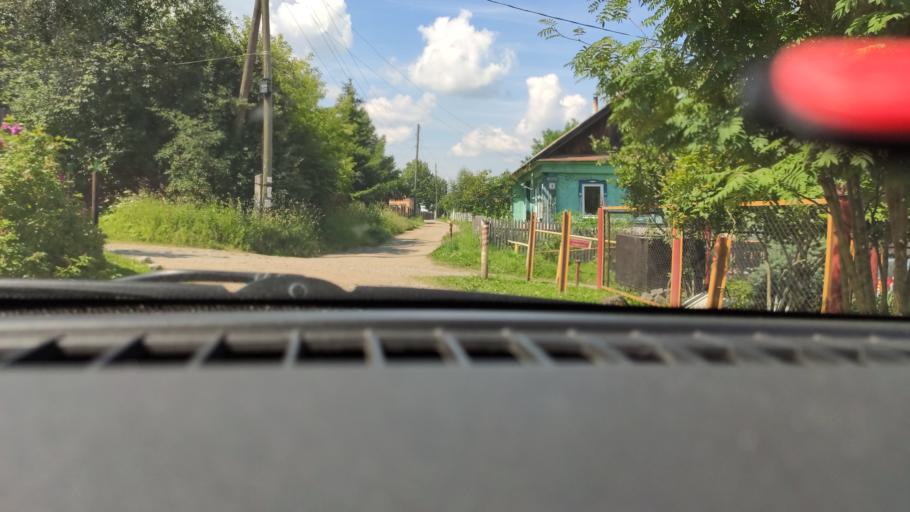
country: RU
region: Perm
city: Sylva
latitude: 58.0477
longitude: 56.7232
